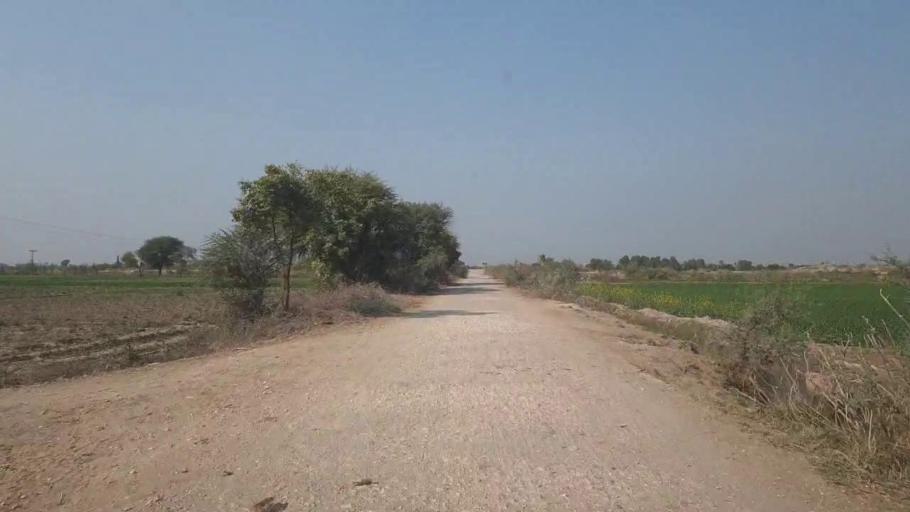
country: PK
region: Sindh
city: Tando Allahyar
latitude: 25.4431
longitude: 68.7873
